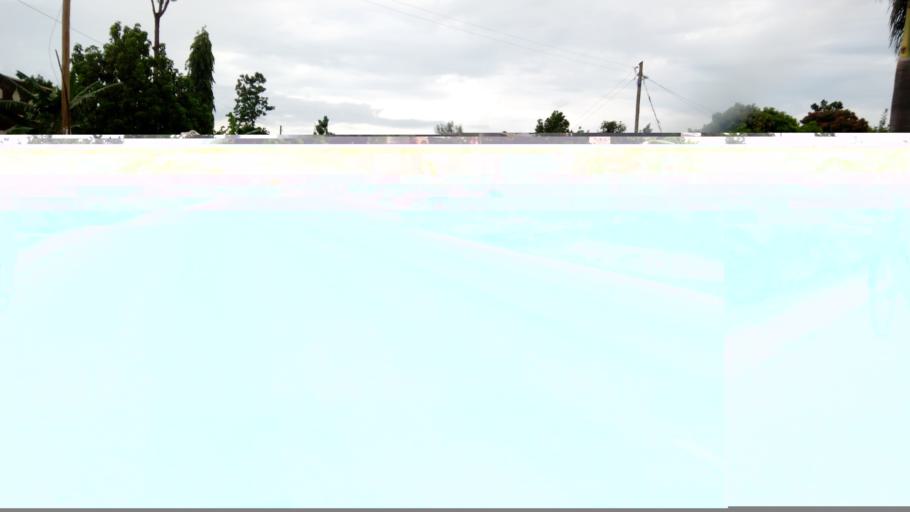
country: UG
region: Eastern Region
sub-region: Mbale District
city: Mbale
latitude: 1.0261
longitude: 34.1769
